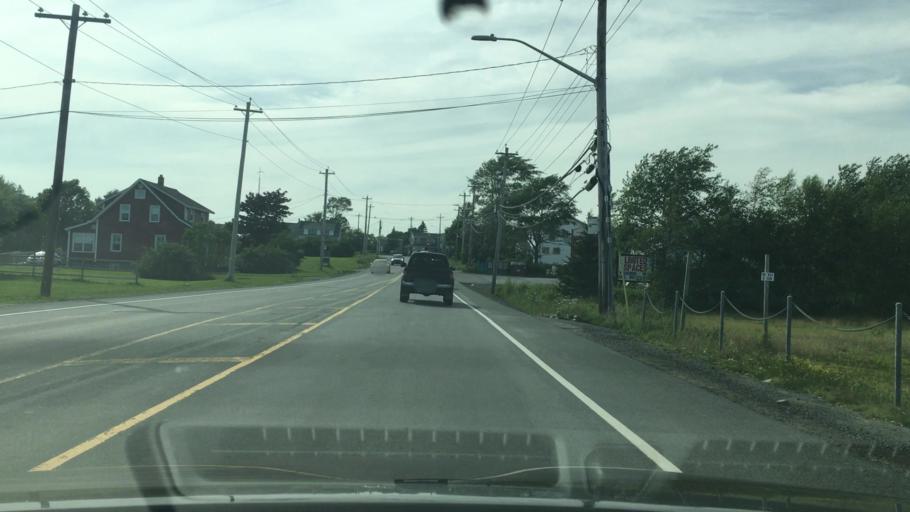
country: CA
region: Nova Scotia
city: Dartmouth
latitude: 44.7328
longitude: -63.7608
